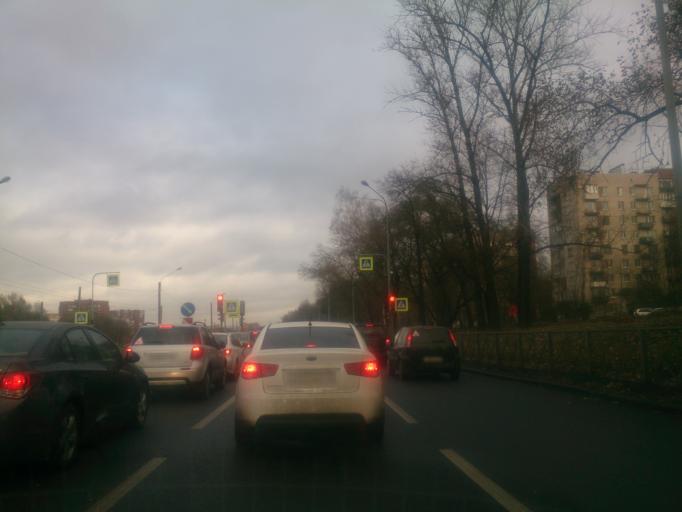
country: RU
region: St.-Petersburg
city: Dachnoye
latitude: 59.8555
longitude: 30.2466
